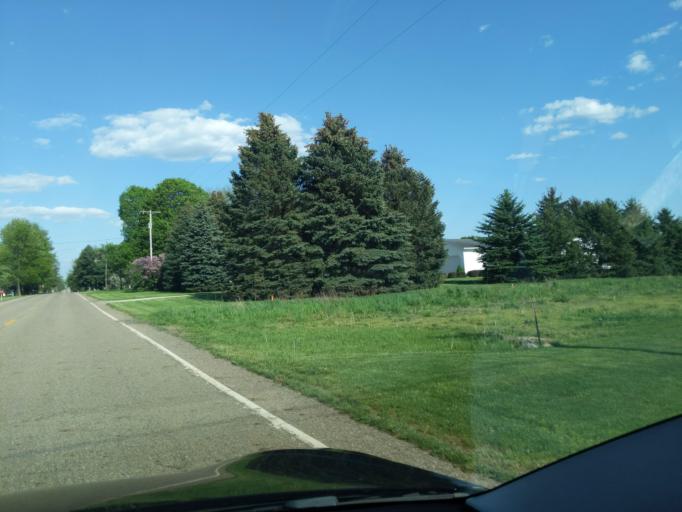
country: US
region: Michigan
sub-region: Eaton County
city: Dimondale
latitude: 42.6828
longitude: -84.6951
